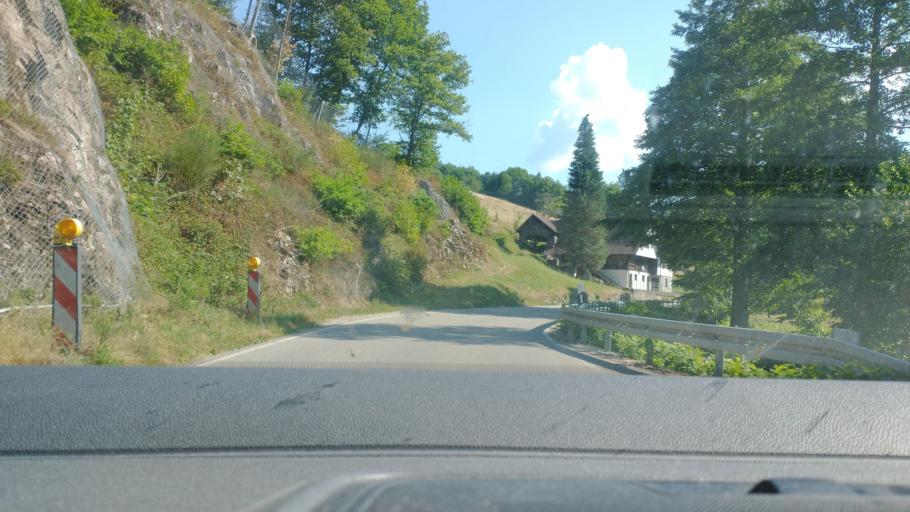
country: DE
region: Baden-Wuerttemberg
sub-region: Freiburg Region
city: Nordrach
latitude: 48.4060
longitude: 8.0964
